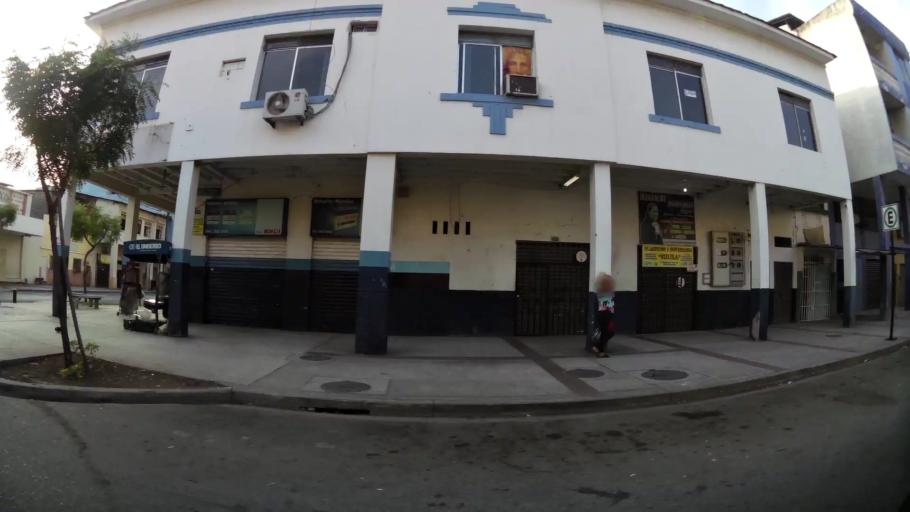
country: EC
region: Guayas
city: Guayaquil
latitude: -2.2014
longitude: -79.8981
